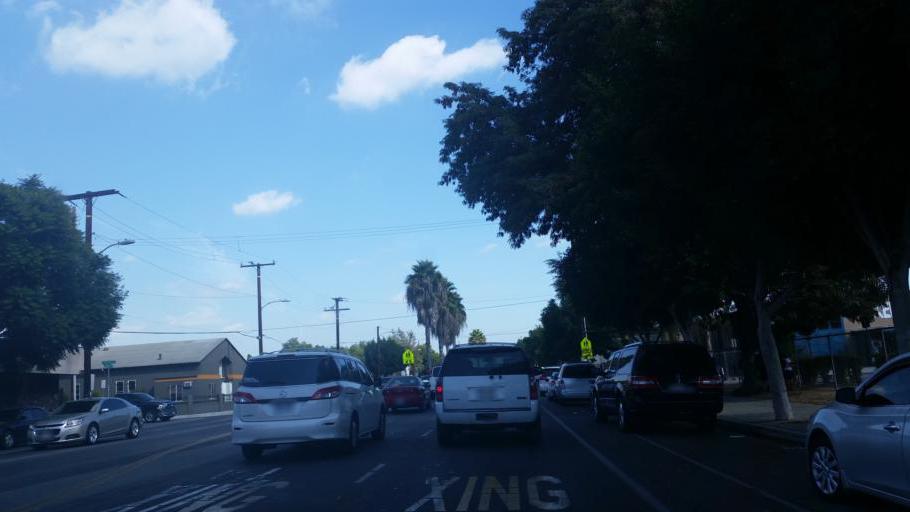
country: US
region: California
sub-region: Los Angeles County
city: East Rancho Dominguez
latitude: 33.8887
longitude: -118.1979
